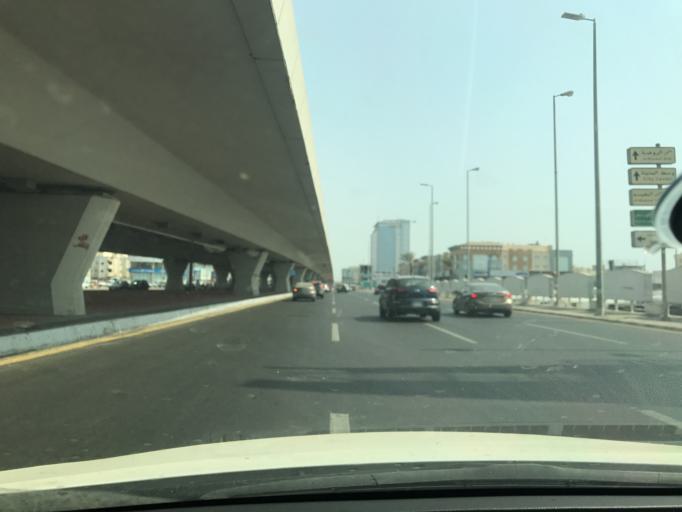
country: SA
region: Makkah
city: Jeddah
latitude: 21.6158
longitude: 39.1550
